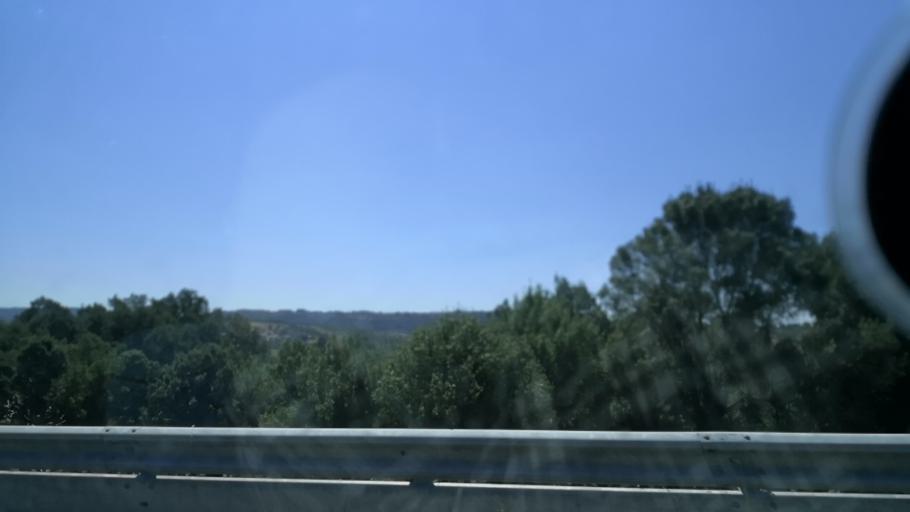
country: PT
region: Braganca
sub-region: Macedo de Cavaleiros
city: Macedo de Cavaleiros
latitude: 41.6223
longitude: -6.8625
